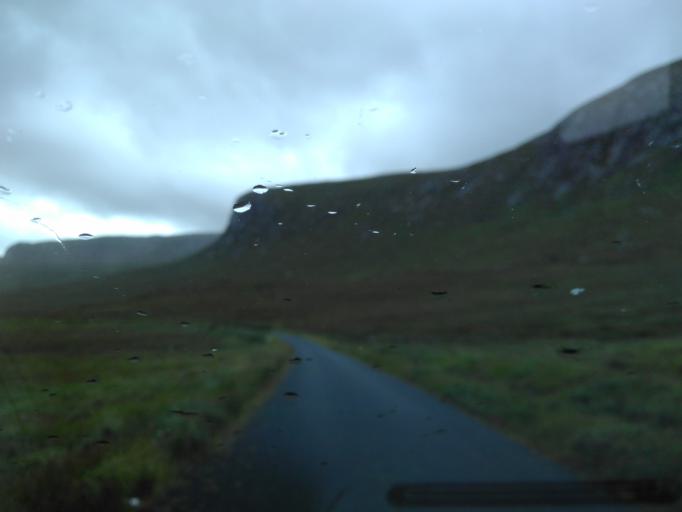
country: IE
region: Ulster
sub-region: County Donegal
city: Dunlewy
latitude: 54.9721
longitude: -8.0871
